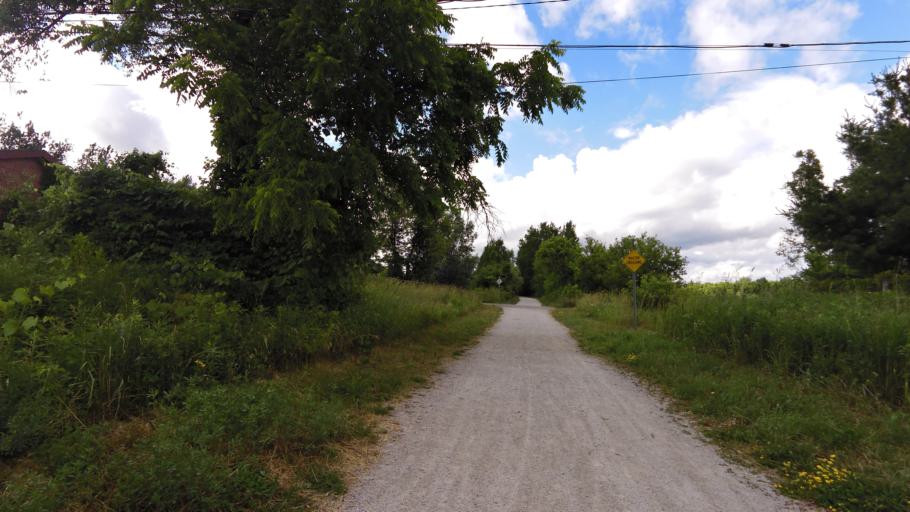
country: CA
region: Ontario
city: Brampton
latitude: 43.7985
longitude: -79.9316
